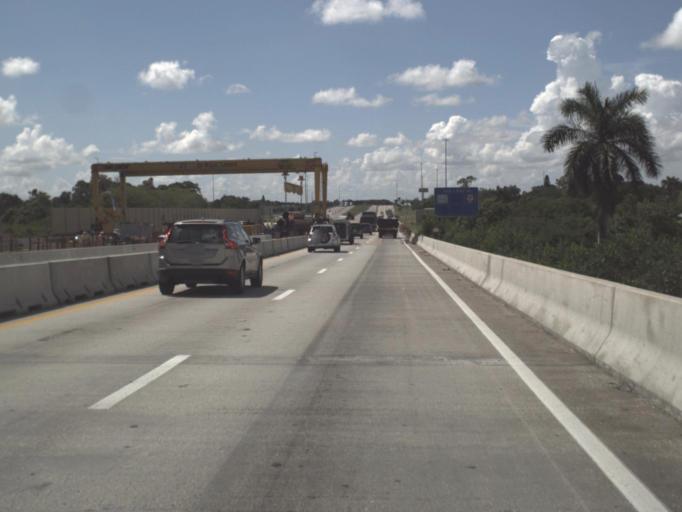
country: US
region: Florida
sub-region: Lee County
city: Tice
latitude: 26.6924
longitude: -81.7991
